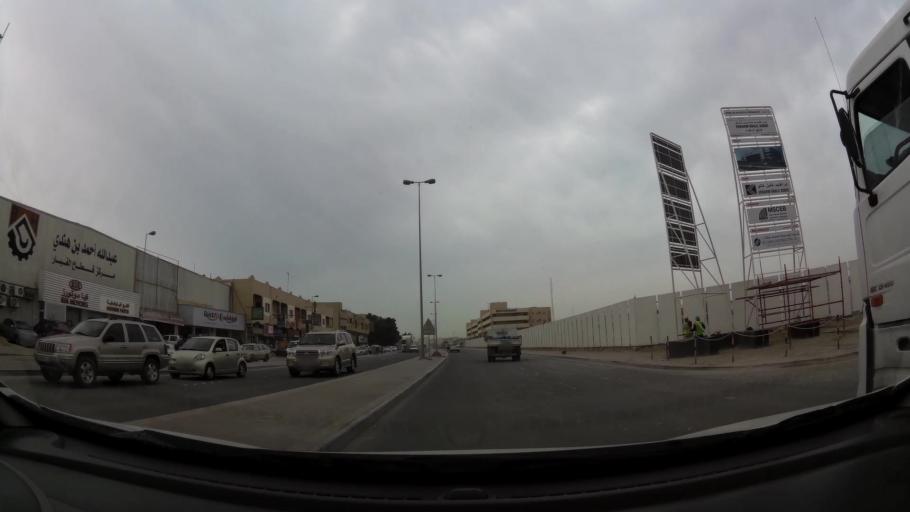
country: BH
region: Northern
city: Madinat `Isa
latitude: 26.1870
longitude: 50.5328
